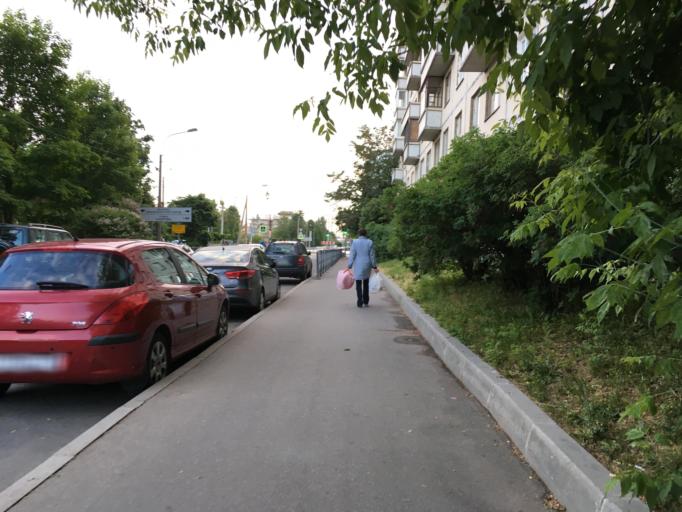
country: RU
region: St.-Petersburg
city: Staraya Derevnya
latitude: 60.0160
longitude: 30.2419
